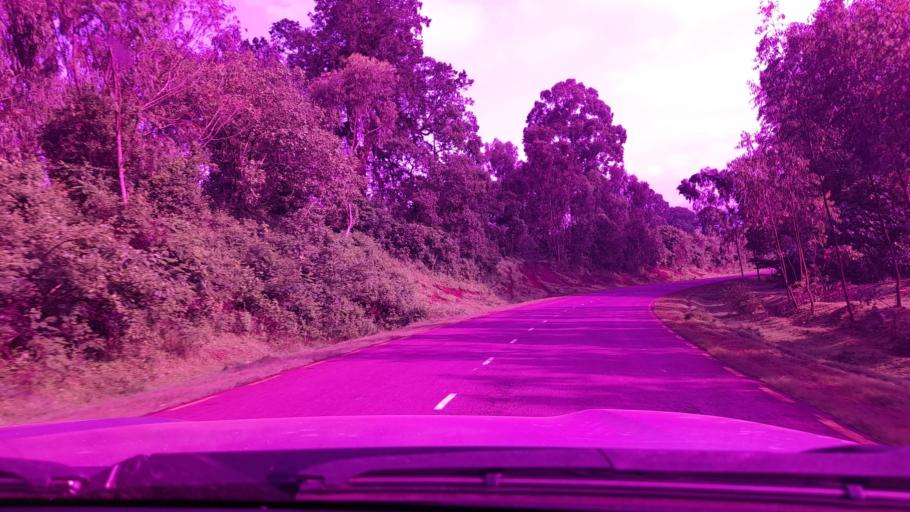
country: ET
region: Oromiya
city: Bedele
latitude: 8.1911
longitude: 36.4437
